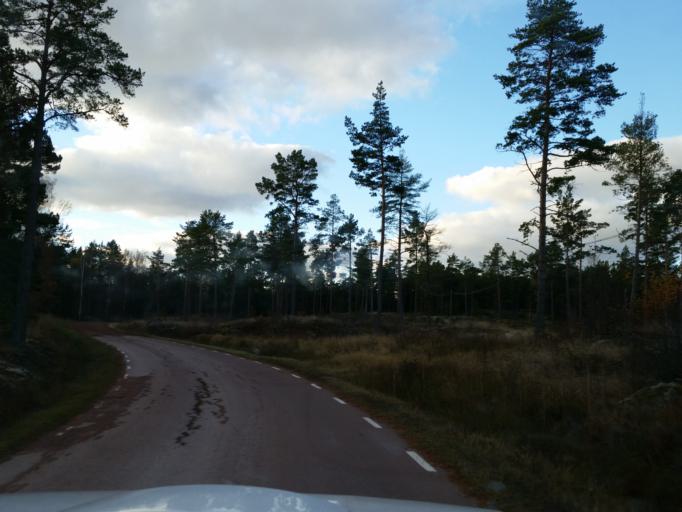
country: AX
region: Alands skaergard
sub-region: Foegloe
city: Foegloe
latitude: 59.9998
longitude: 20.3519
